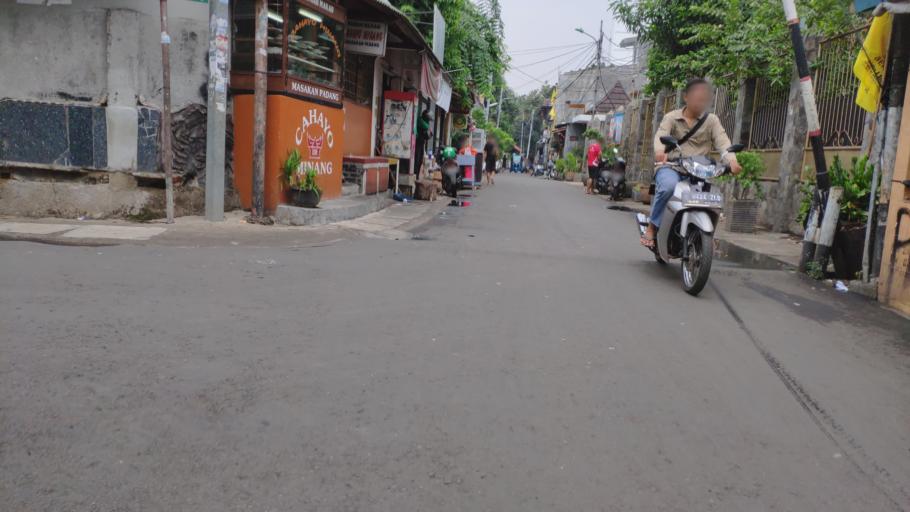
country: ID
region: Jakarta Raya
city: Jakarta
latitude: -6.2016
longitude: 106.8573
